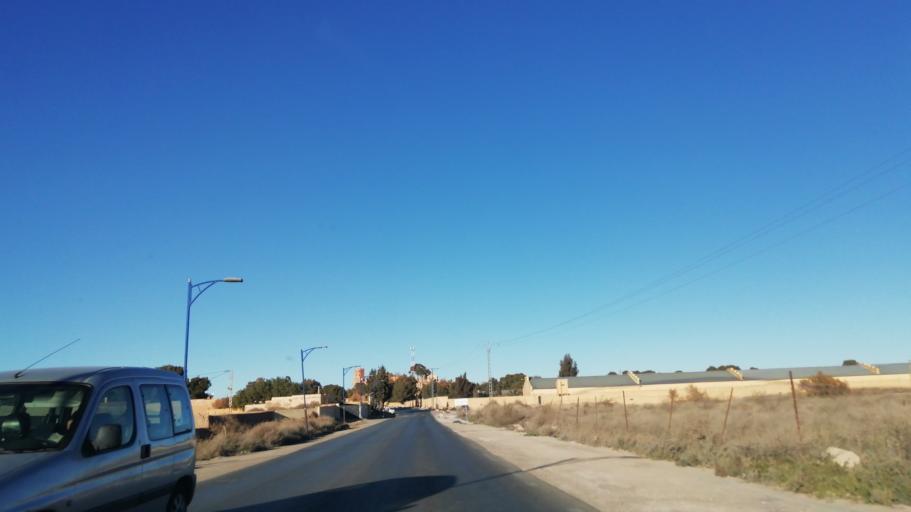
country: DZ
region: Saida
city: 'Ain el Hadjar
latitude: 34.1419
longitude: 0.0710
